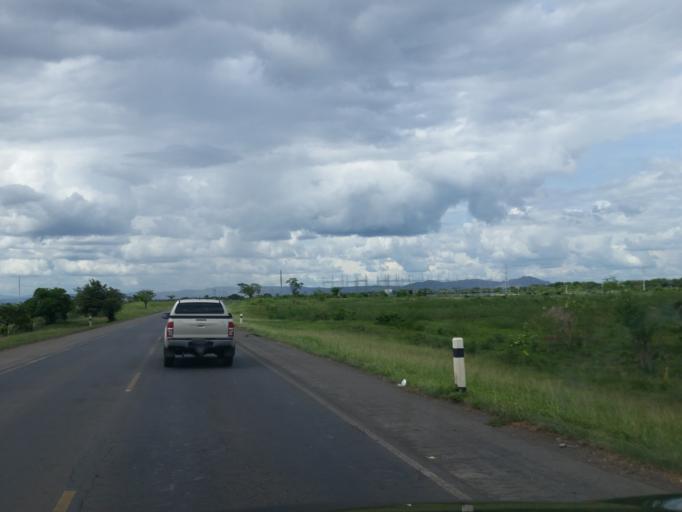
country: NI
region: Managua
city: Tipitapa
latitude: 12.2504
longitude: -86.0880
